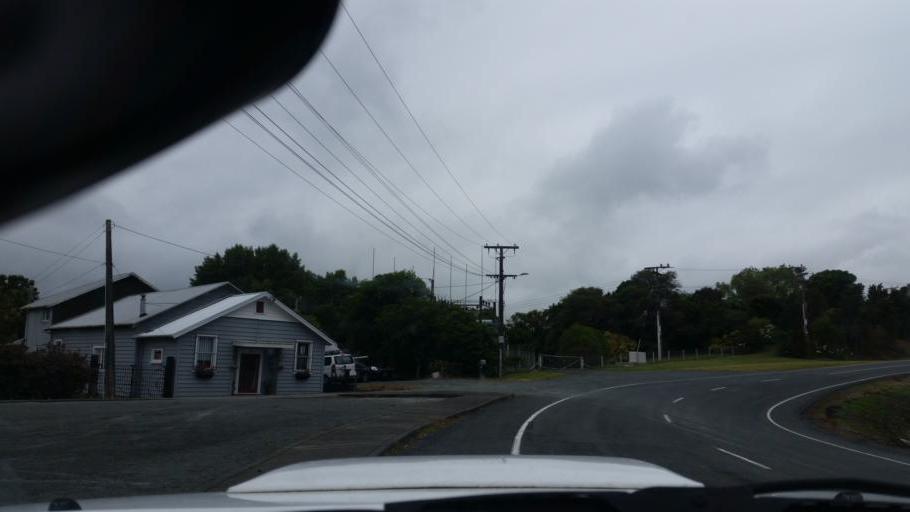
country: NZ
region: Auckland
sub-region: Auckland
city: Wellsford
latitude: -36.1598
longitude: 174.4473
